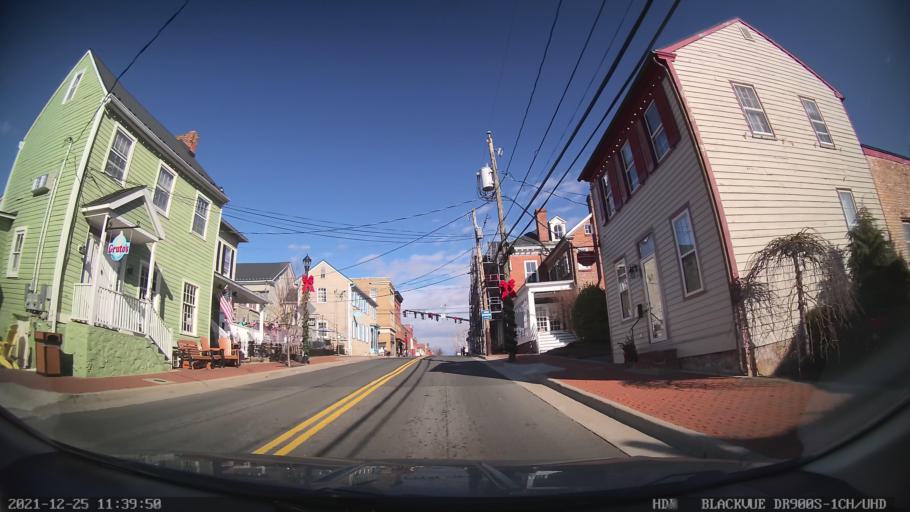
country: US
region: Virginia
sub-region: Loudoun County
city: Leesburg
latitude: 39.1137
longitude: -77.5653
